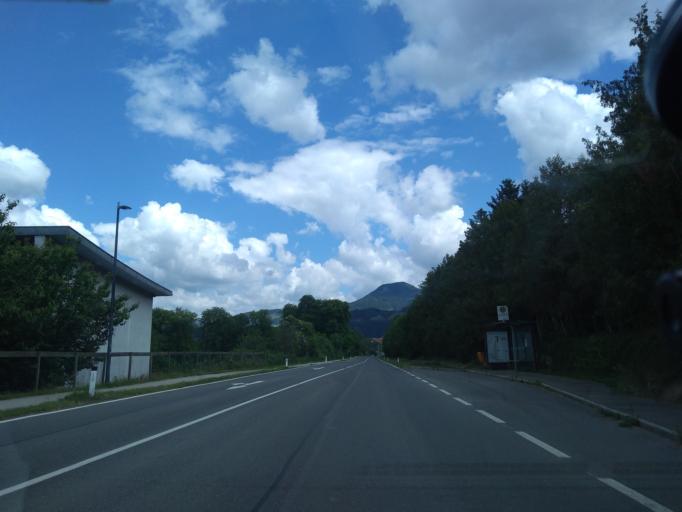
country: AT
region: Styria
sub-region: Politischer Bezirk Graz-Umgebung
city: Frohnleiten
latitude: 47.2582
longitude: 15.3211
